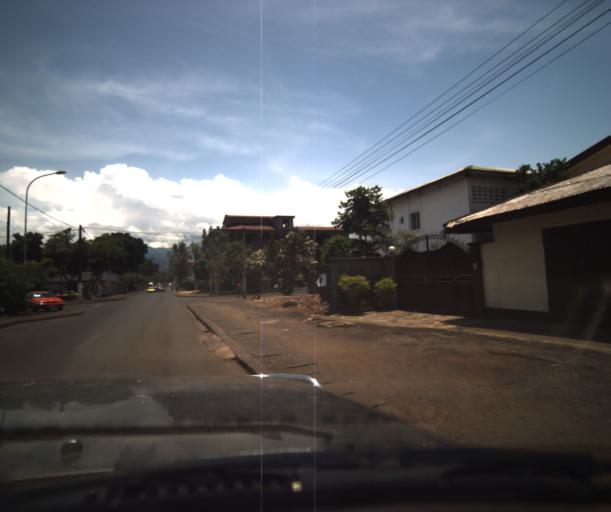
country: CM
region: South-West Province
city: Limbe
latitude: 4.0076
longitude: 9.2097
